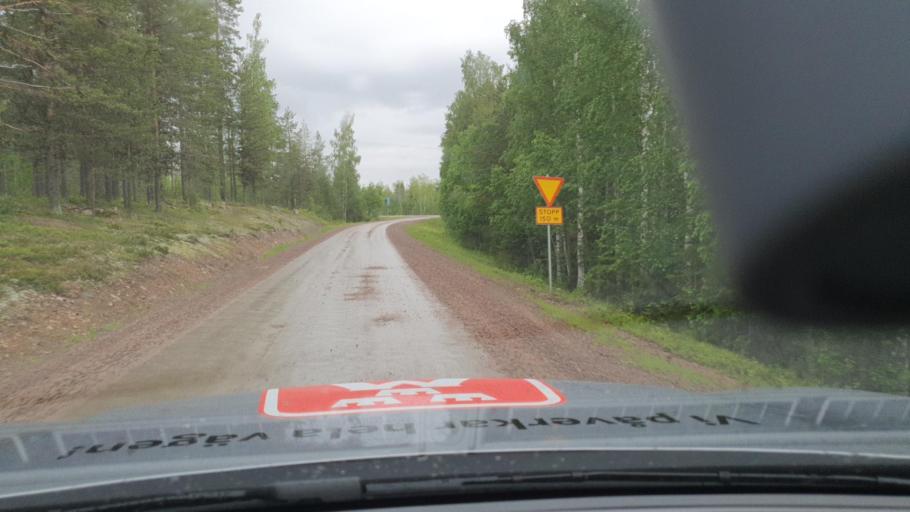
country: SE
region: Norrbotten
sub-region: Overkalix Kommun
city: OEverkalix
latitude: 66.6472
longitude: 22.7000
